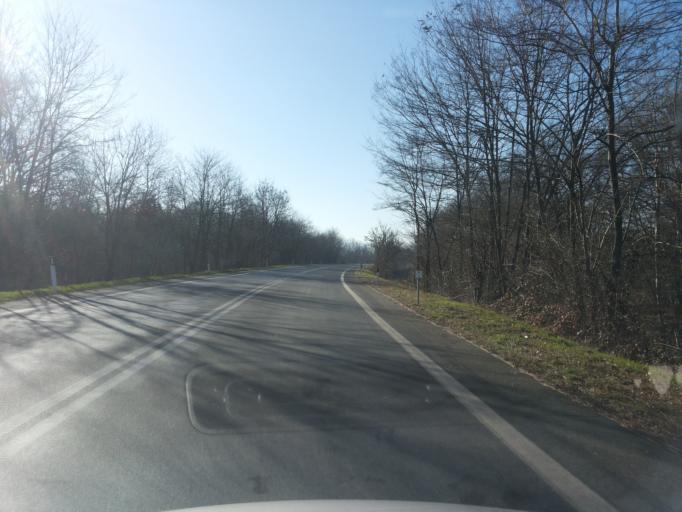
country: IT
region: Piedmont
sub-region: Provincia di Biella
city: Verrone
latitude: 45.4940
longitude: 8.1254
